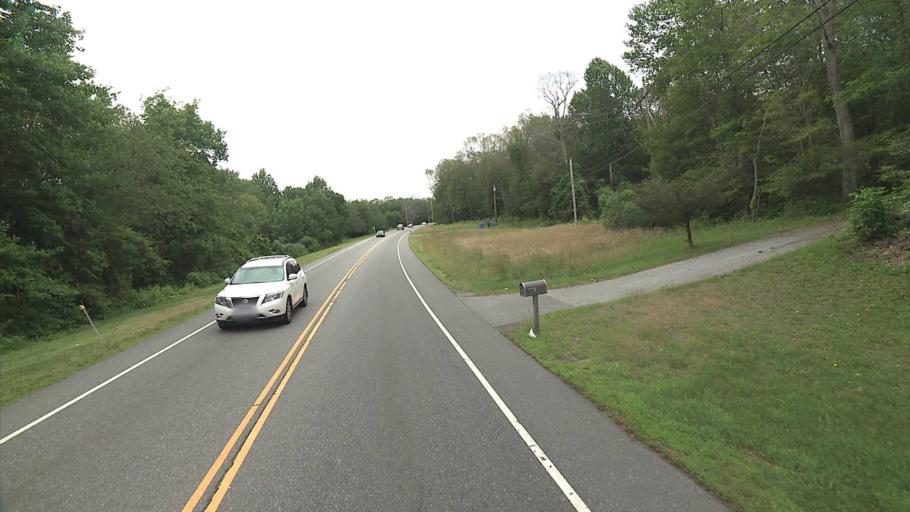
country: US
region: Connecticut
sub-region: New London County
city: Ledyard Center
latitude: 41.4030
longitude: -72.0251
